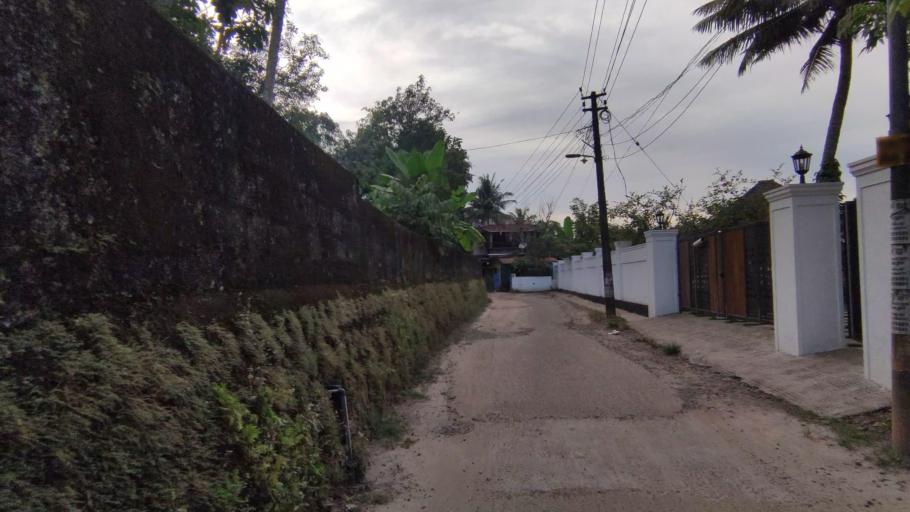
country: IN
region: Kerala
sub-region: Kottayam
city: Kottayam
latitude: 9.6360
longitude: 76.5086
